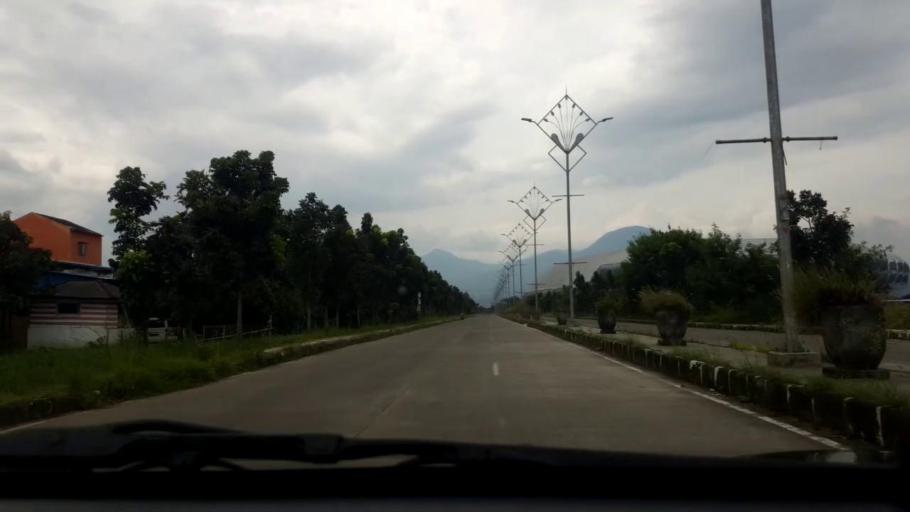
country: ID
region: West Java
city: Cileunyi
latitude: -6.9623
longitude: 107.7097
